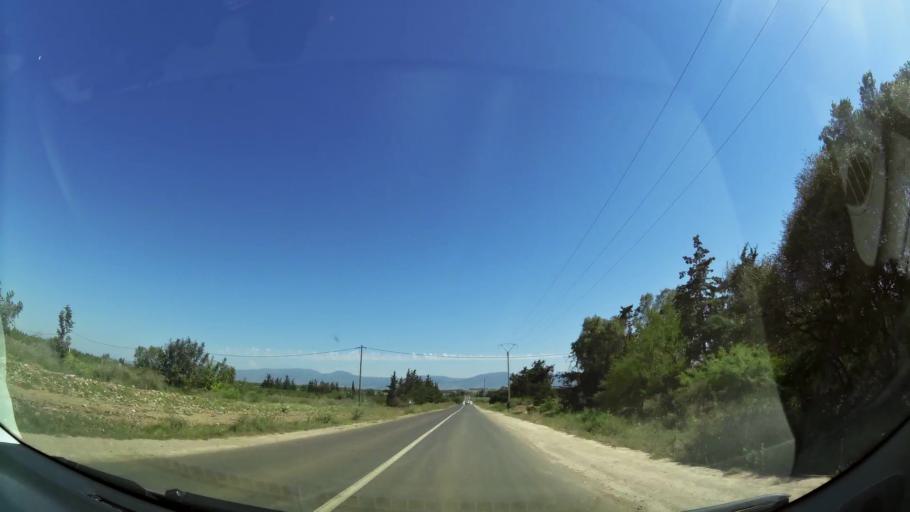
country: MA
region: Oriental
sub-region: Berkane-Taourirt
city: Madagh
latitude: 35.0265
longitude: -2.4112
